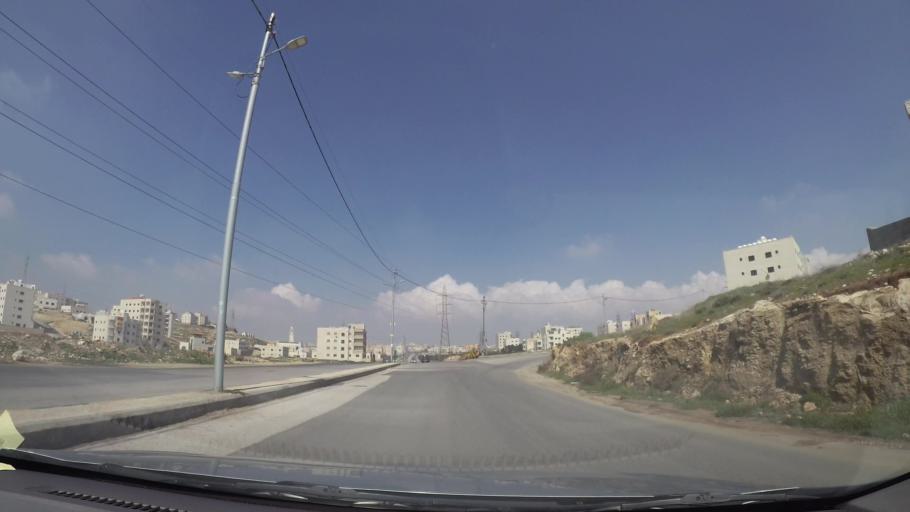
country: JO
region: Amman
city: Al Bunayyat ash Shamaliyah
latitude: 31.8882
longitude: 35.9024
